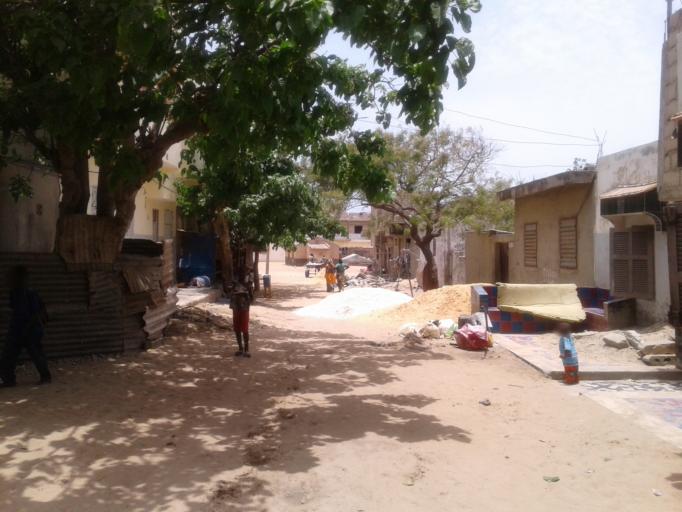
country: SN
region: Dakar
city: Pikine
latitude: 14.7830
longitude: -17.3753
